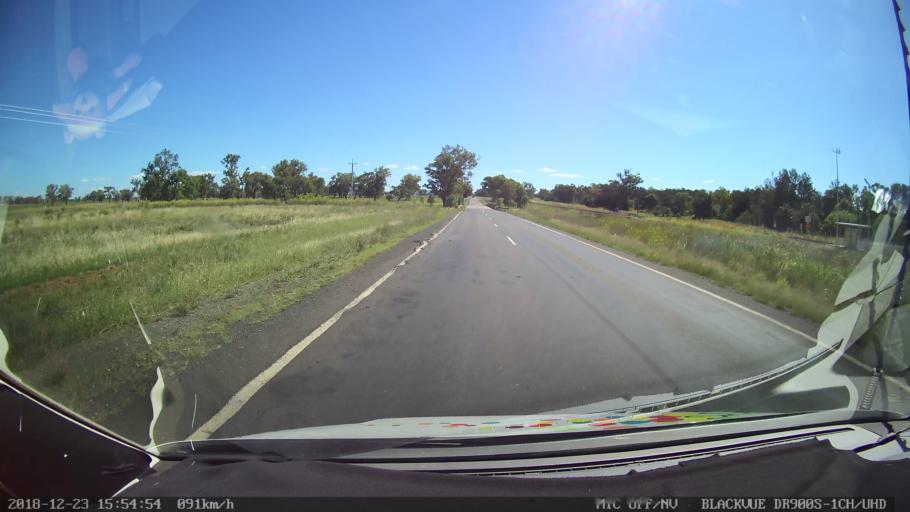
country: AU
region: New South Wales
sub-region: Tamworth Municipality
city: Phillip
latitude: -31.1498
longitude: 150.8739
